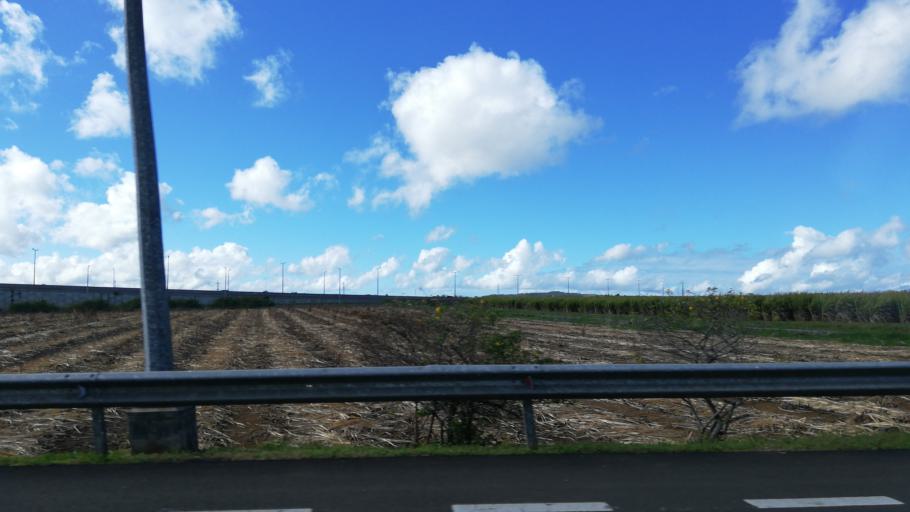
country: MU
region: Moka
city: Verdun
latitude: -20.2290
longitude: 57.5428
